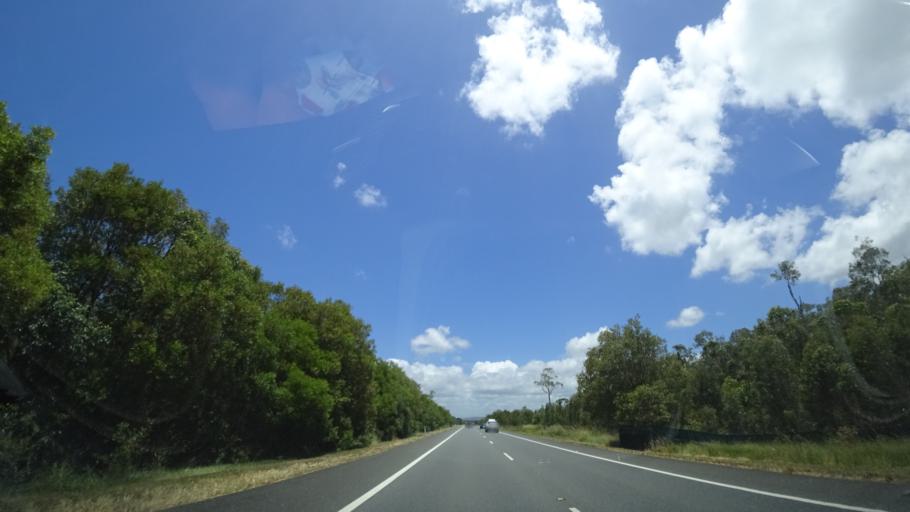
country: AU
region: Queensland
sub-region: Sunshine Coast
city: Little Mountain
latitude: -26.7666
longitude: 153.0951
